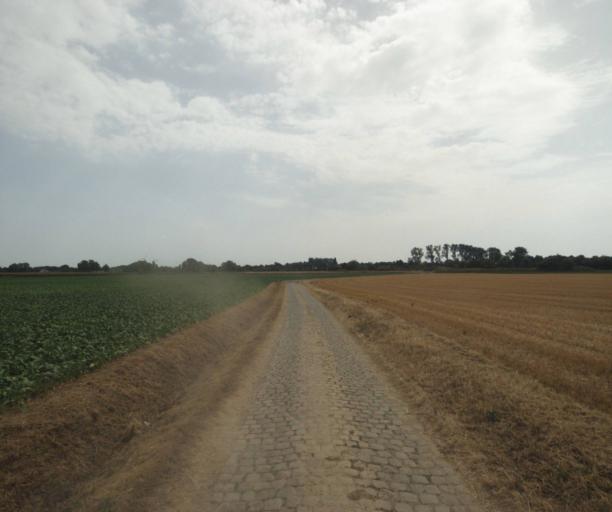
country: BE
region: Wallonia
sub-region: Province du Hainaut
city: Estaimpuis
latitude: 50.6960
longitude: 3.2549
